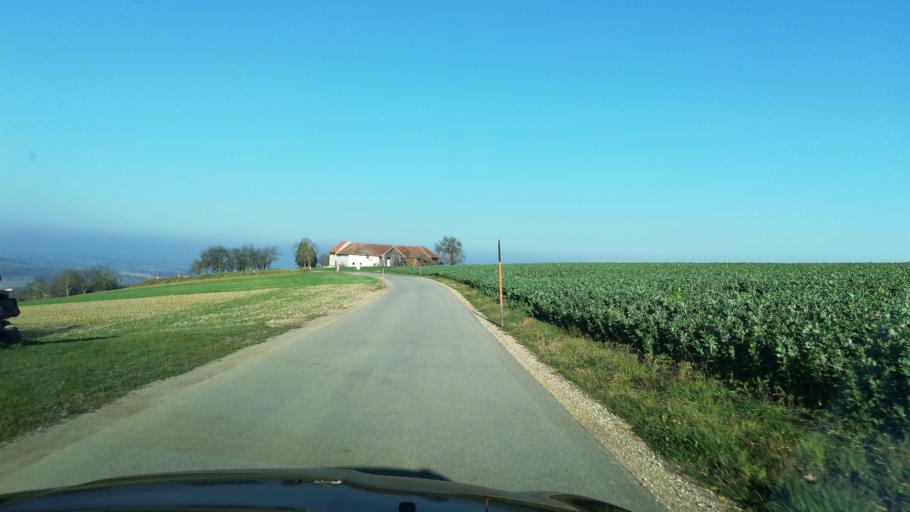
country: AT
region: Upper Austria
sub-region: Wels-Land
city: Buchkirchen
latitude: 48.2537
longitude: 14.0158
